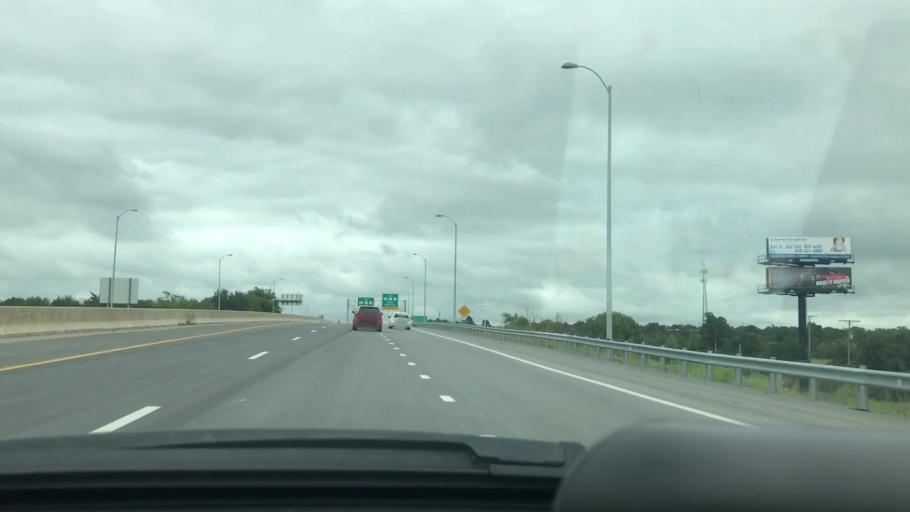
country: US
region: Oklahoma
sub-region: Pittsburg County
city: Krebs
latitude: 34.9225
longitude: -95.7433
